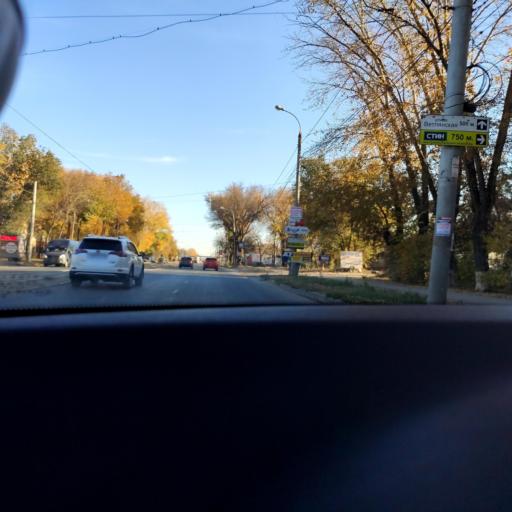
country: RU
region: Samara
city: Smyshlyayevka
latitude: 53.1957
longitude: 50.2904
